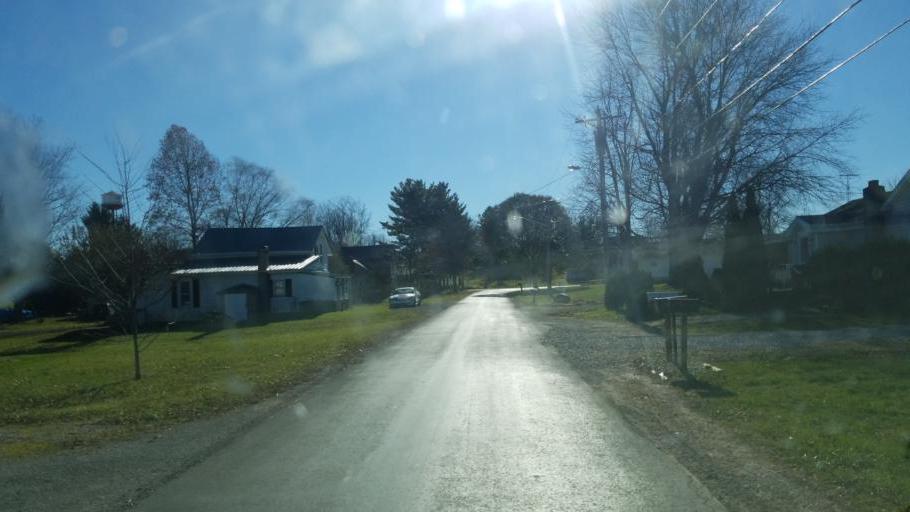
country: US
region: Ohio
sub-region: Huron County
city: Plymouth
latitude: 40.9712
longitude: -82.6034
